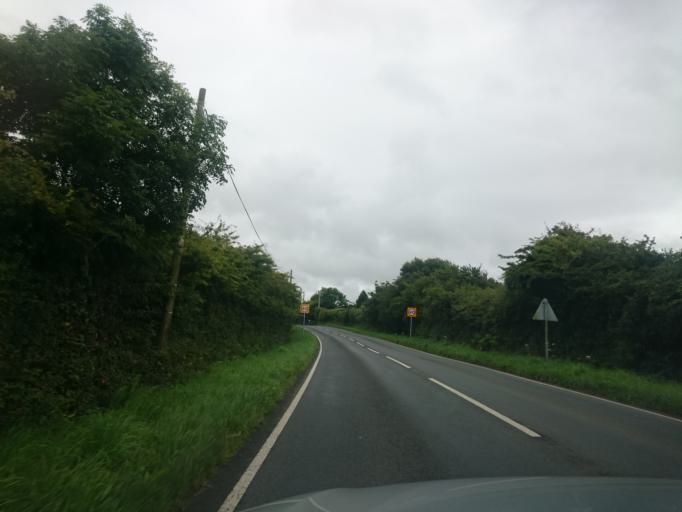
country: GB
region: Wales
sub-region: Pembrokeshire
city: Freystrop
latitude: 51.7751
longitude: -4.9661
